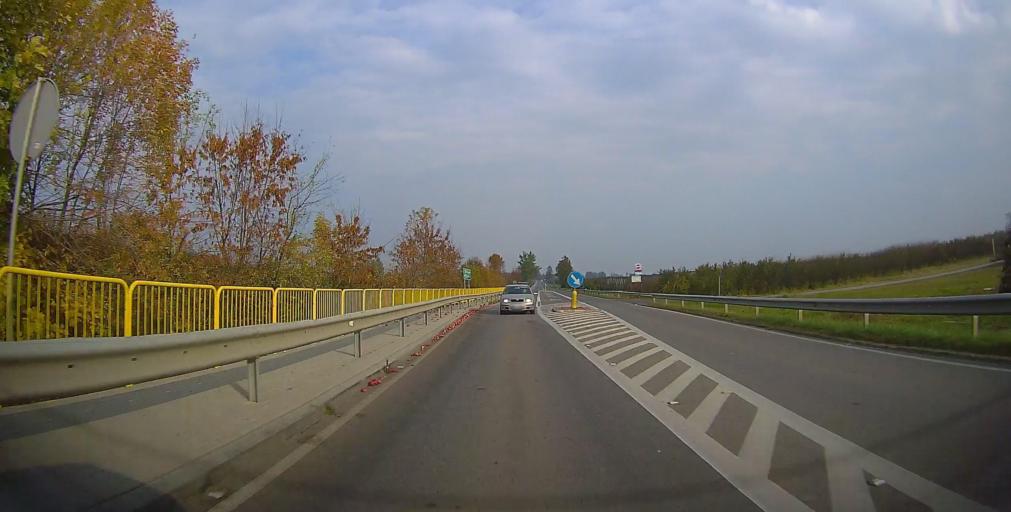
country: PL
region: Masovian Voivodeship
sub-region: Powiat grojecki
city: Bledow
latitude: 51.7658
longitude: 20.7678
